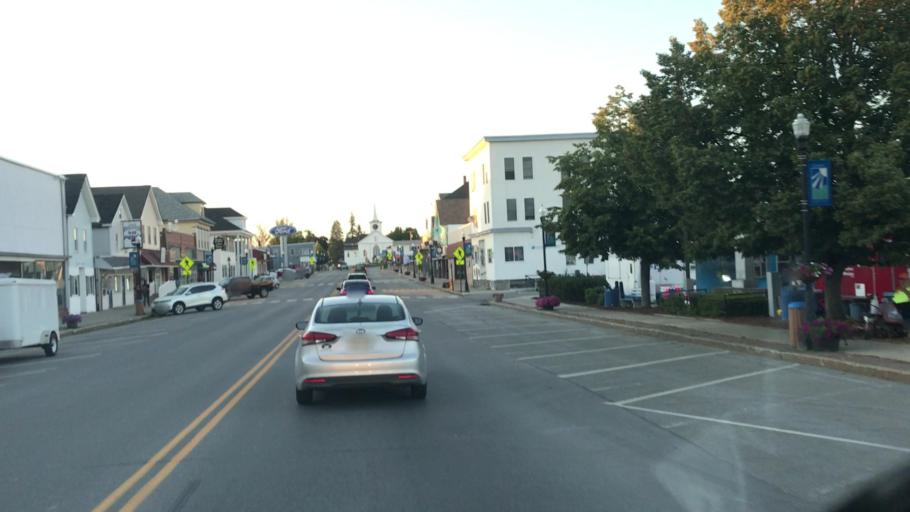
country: US
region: Maine
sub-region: Penobscot County
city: Lincoln
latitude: 45.3629
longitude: -68.5042
